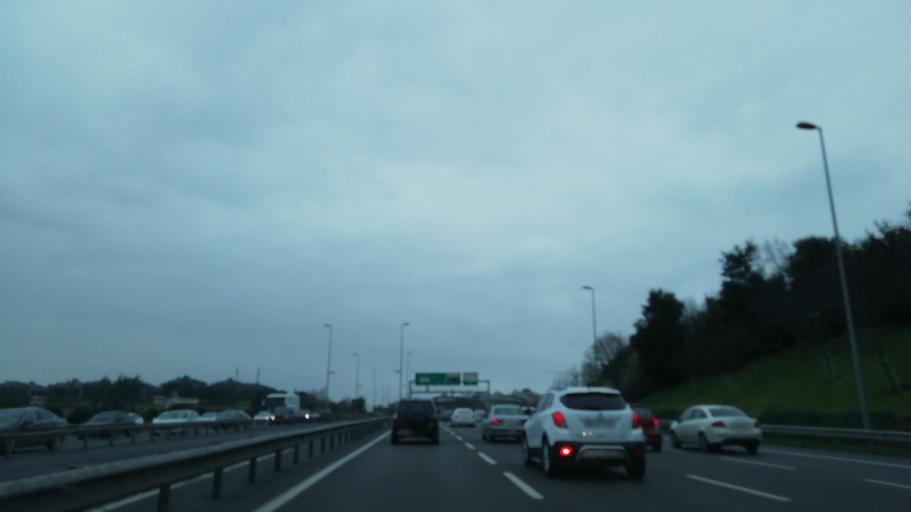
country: TR
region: Istanbul
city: UEskuedar
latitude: 41.0307
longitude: 29.0455
